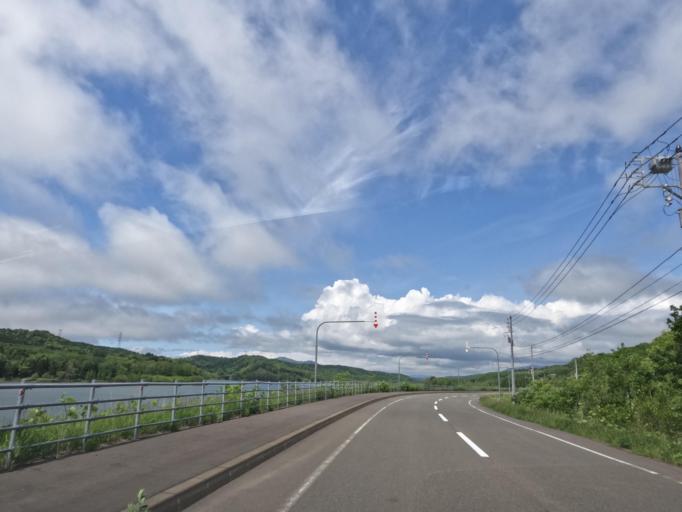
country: JP
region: Hokkaido
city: Tobetsu
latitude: 43.3605
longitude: 141.5683
